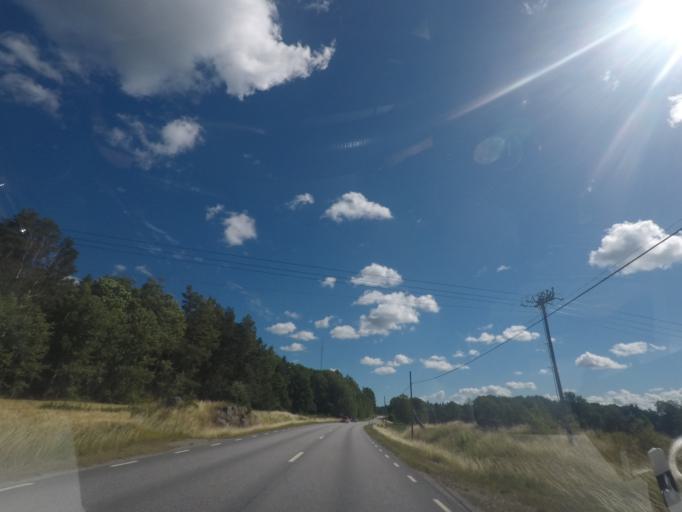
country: SE
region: Stockholm
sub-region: Norrtalje Kommun
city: Skanninge
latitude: 59.8951
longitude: 18.4411
